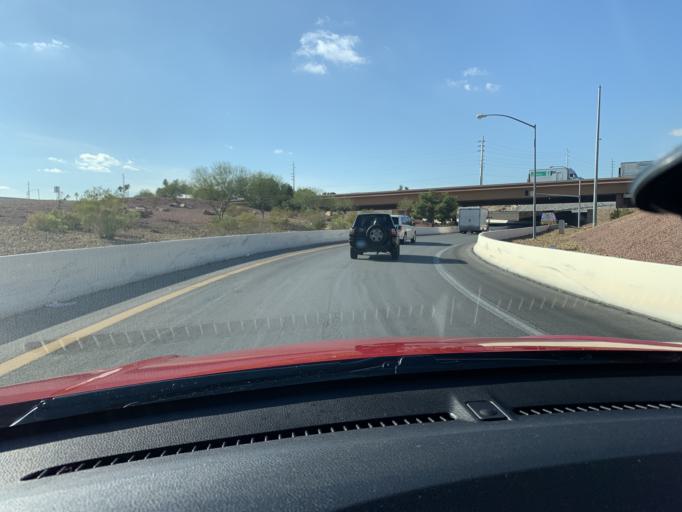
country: US
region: Nevada
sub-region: Clark County
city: Winchester
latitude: 36.1129
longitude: -115.0812
